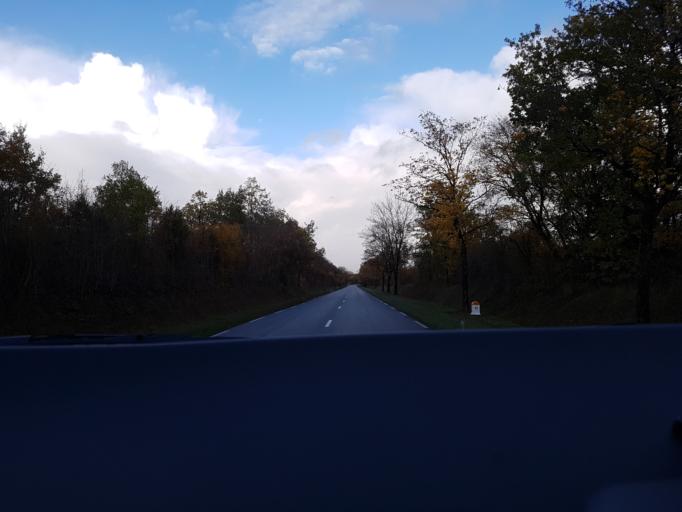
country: FR
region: Poitou-Charentes
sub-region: Departement de la Charente-Maritime
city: Aulnay
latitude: 46.0823
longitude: -0.2982
